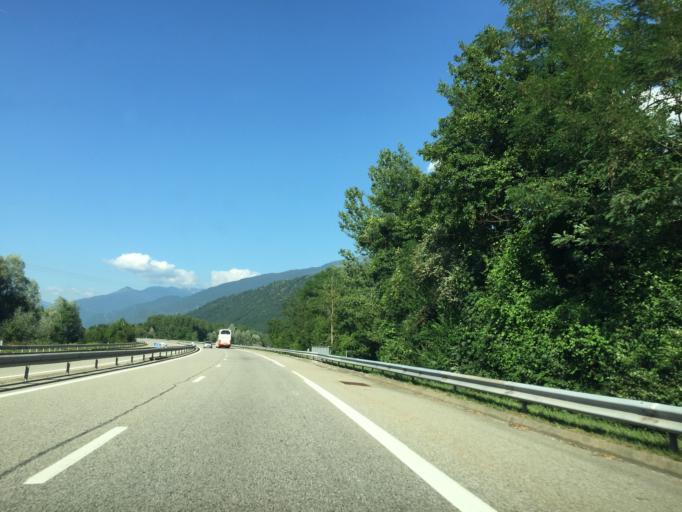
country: FR
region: Rhone-Alpes
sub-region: Departement de la Savoie
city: Aiton
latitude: 45.5801
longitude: 6.2664
